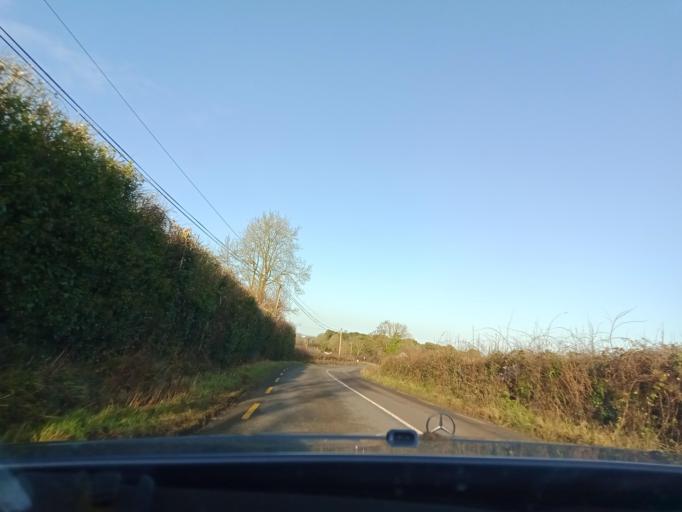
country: IE
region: Leinster
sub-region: Kilkenny
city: Callan
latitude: 52.5240
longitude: -7.3829
